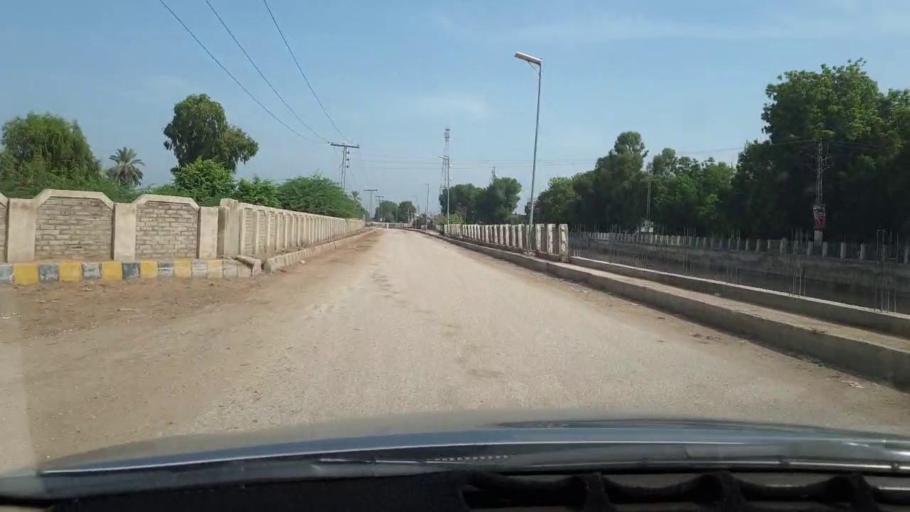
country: PK
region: Sindh
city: Khairpur
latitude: 27.5224
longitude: 68.7560
